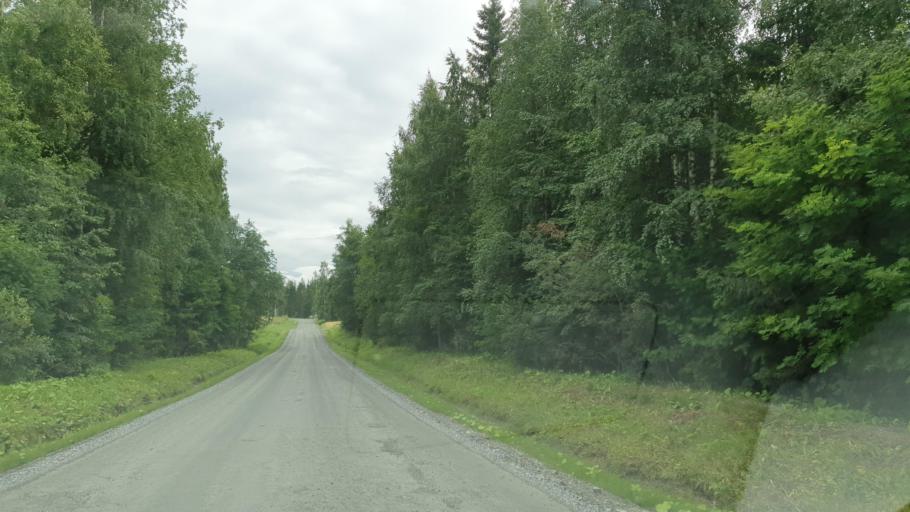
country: FI
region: Northern Savo
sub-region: Ylae-Savo
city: Iisalmi
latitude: 63.5213
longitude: 27.0971
